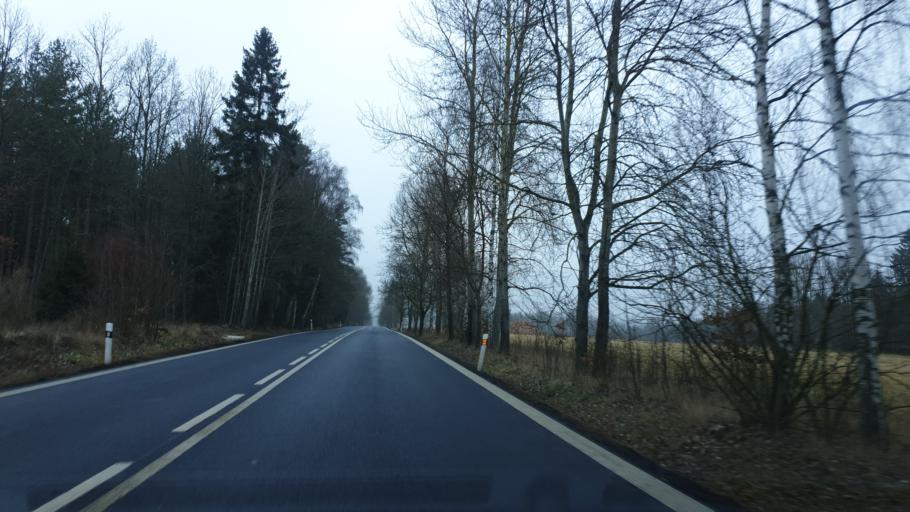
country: CZ
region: Karlovarsky
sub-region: Okres Cheb
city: Skalna
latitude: 50.1526
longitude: 12.3264
